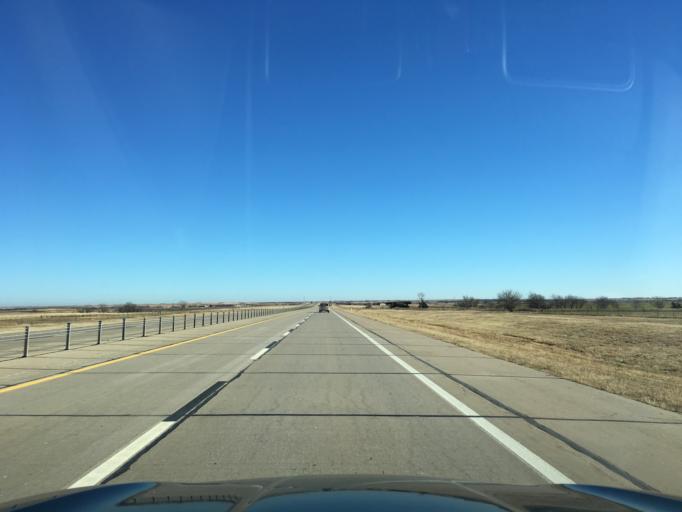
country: US
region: Oklahoma
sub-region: Noble County
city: Perry
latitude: 36.3990
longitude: -97.2909
